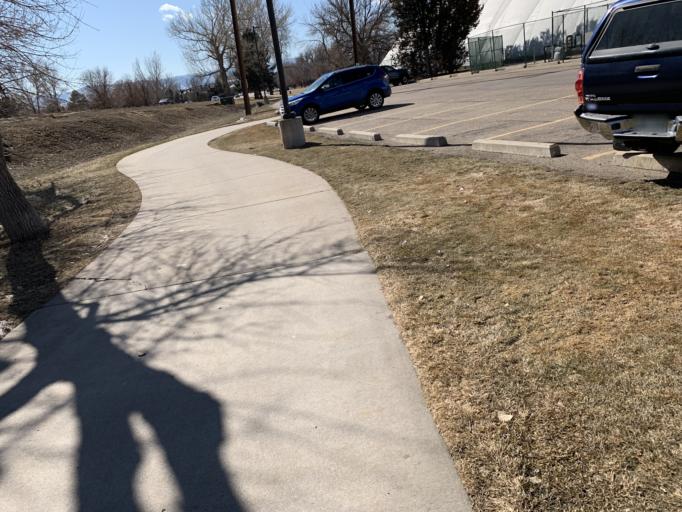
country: US
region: Colorado
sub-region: Arapahoe County
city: Littleton
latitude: 39.6135
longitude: -105.0257
